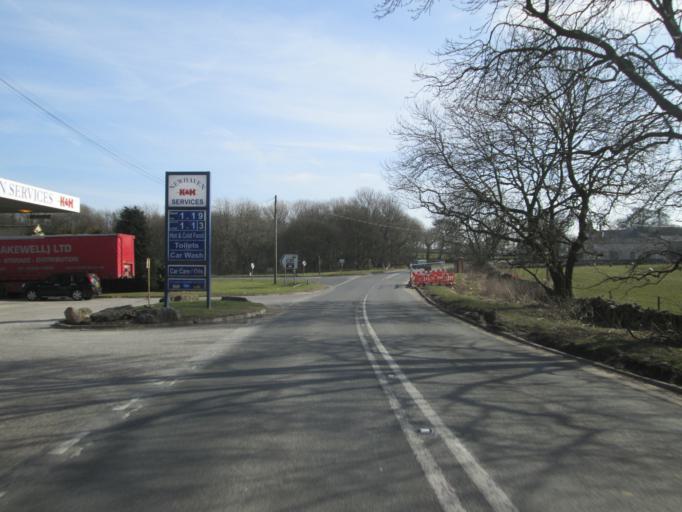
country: GB
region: England
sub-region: Derbyshire
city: Bakewell
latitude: 53.1397
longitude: -1.7537
